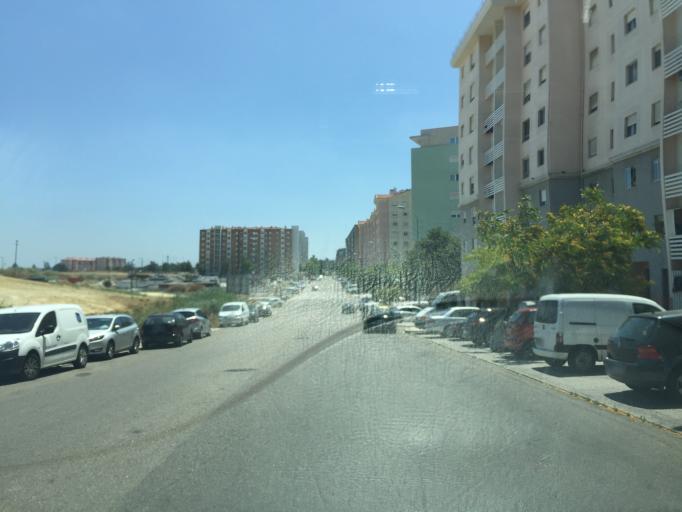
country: PT
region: Lisbon
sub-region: Odivelas
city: Olival do Basto
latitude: 38.7826
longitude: -9.1474
